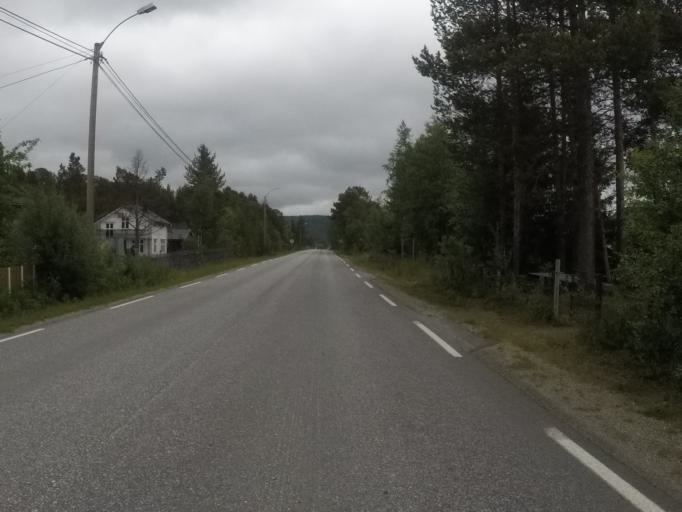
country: NO
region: Finnmark Fylke
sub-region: Karasjok
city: Karasjohka
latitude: 69.4697
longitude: 25.5302
